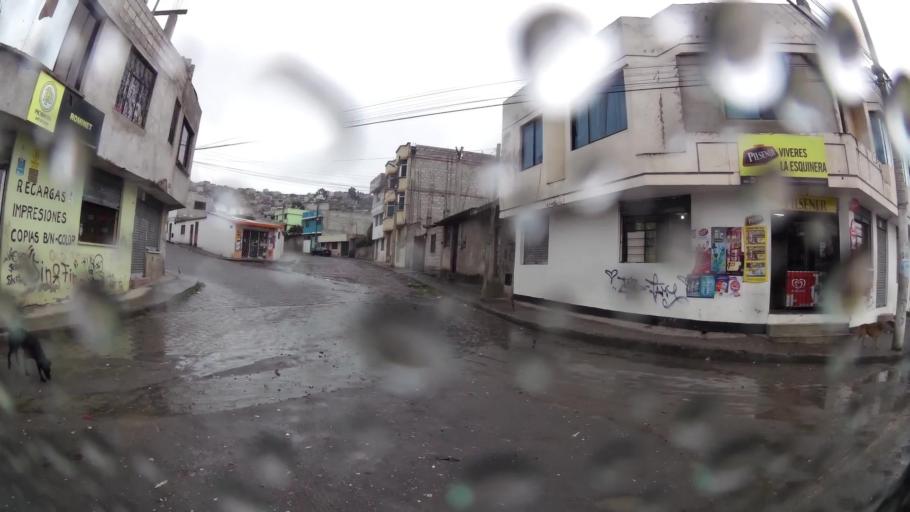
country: EC
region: Pichincha
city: Quito
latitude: -0.0932
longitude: -78.5002
